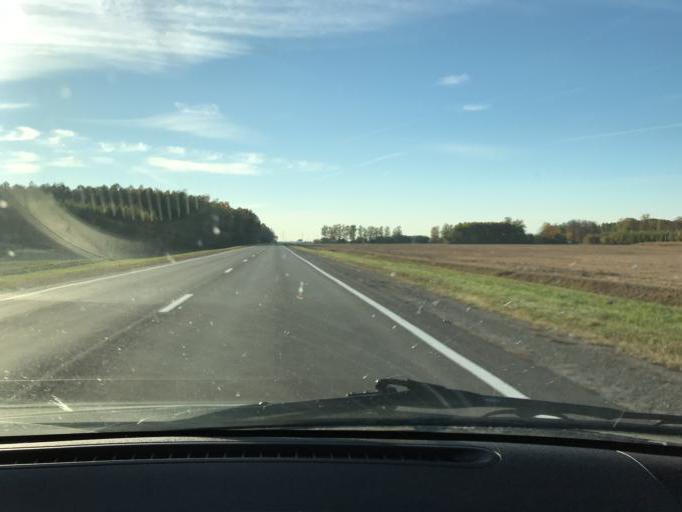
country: BY
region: Brest
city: Antopal'
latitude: 52.2266
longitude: 24.7696
